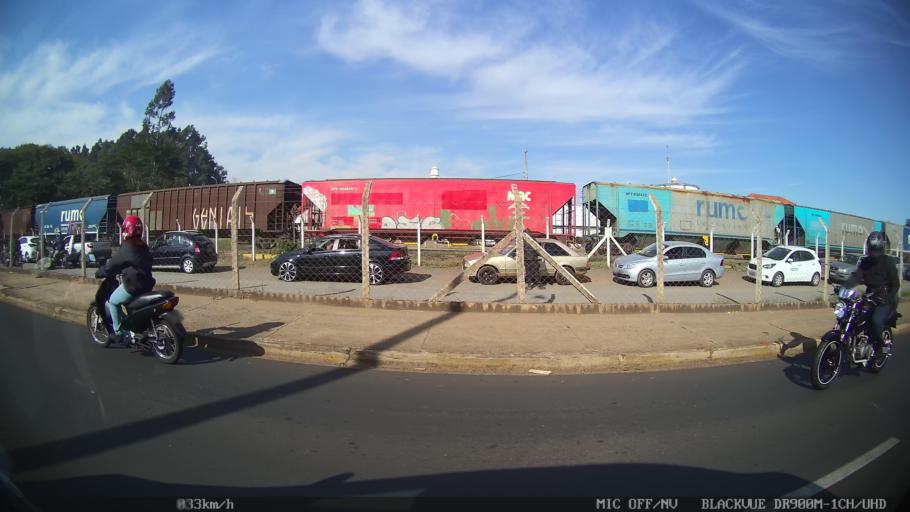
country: BR
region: Sao Paulo
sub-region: Araraquara
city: Araraquara
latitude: -21.7773
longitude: -48.1685
